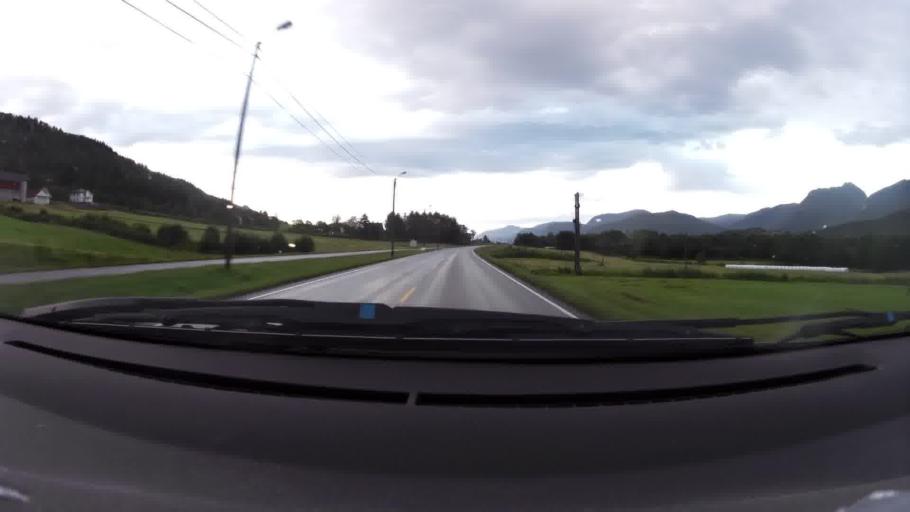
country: NO
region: More og Romsdal
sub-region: Eide
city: Eide
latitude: 62.8920
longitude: 7.3724
